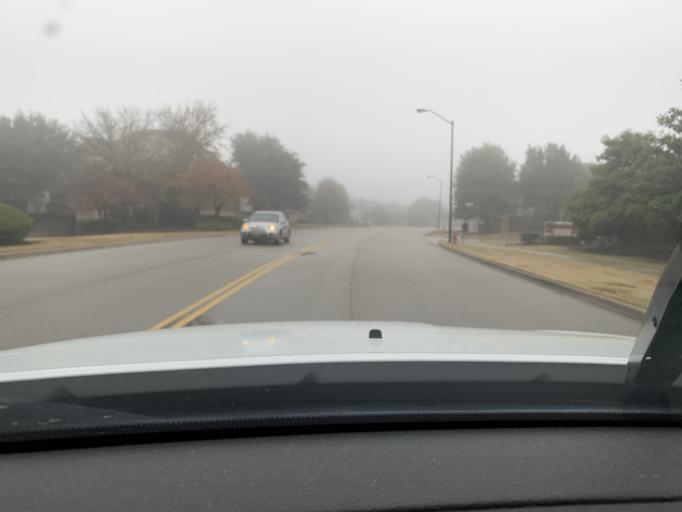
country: US
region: Texas
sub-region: Williamson County
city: Round Rock
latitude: 30.5665
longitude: -97.6785
